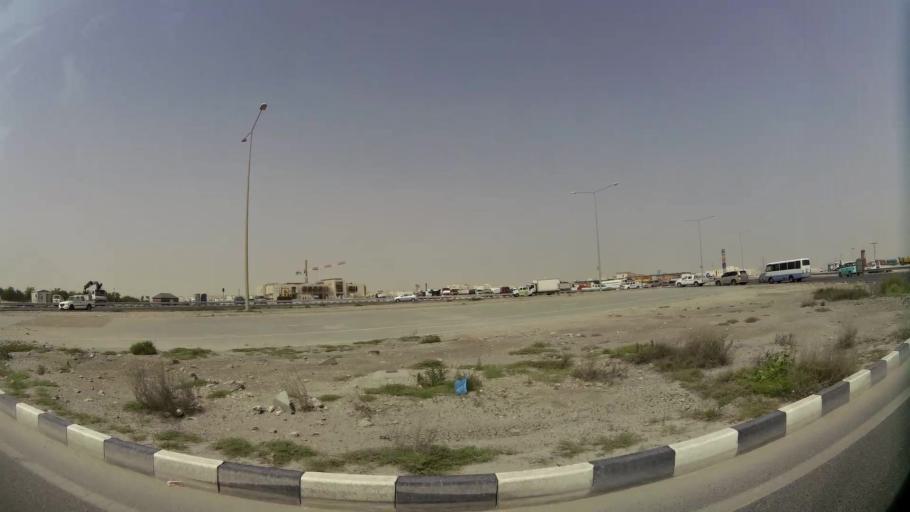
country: QA
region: Baladiyat ar Rayyan
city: Ar Rayyan
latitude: 25.2318
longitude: 51.3946
